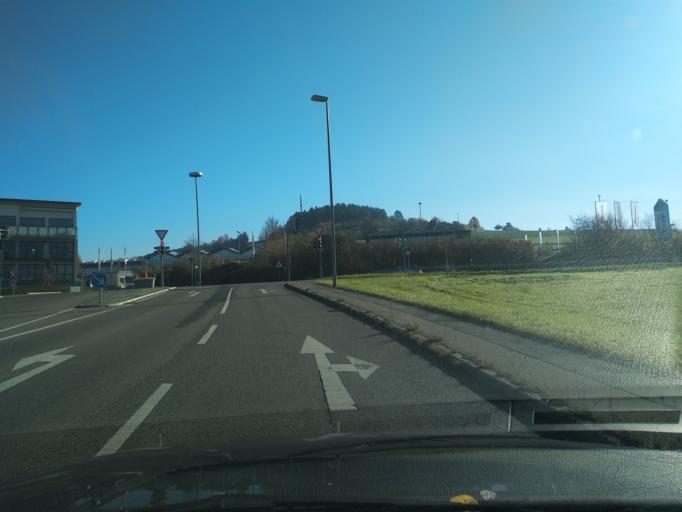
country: DE
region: Baden-Wuerttemberg
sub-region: Karlsruhe Region
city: Calw
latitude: 48.7034
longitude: 8.7593
